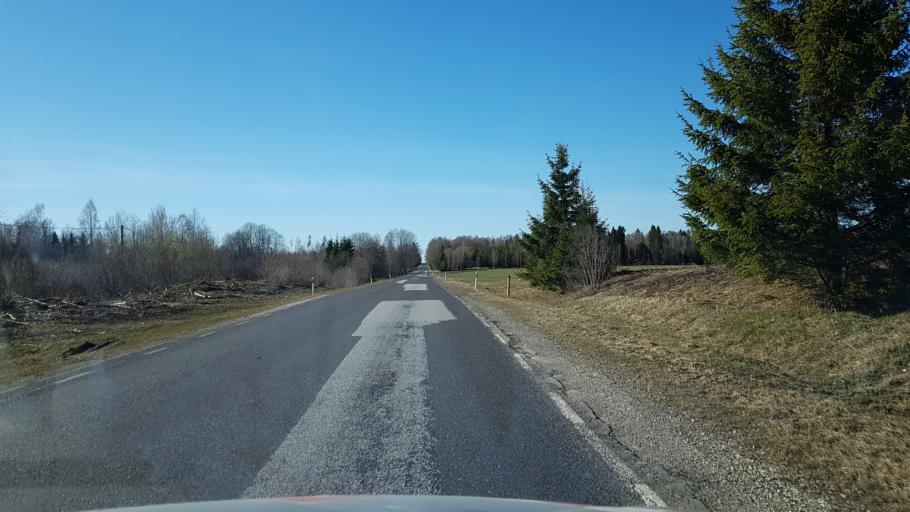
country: EE
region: Laeaene-Virumaa
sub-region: Vinni vald
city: Vinni
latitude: 59.3119
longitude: 26.5219
